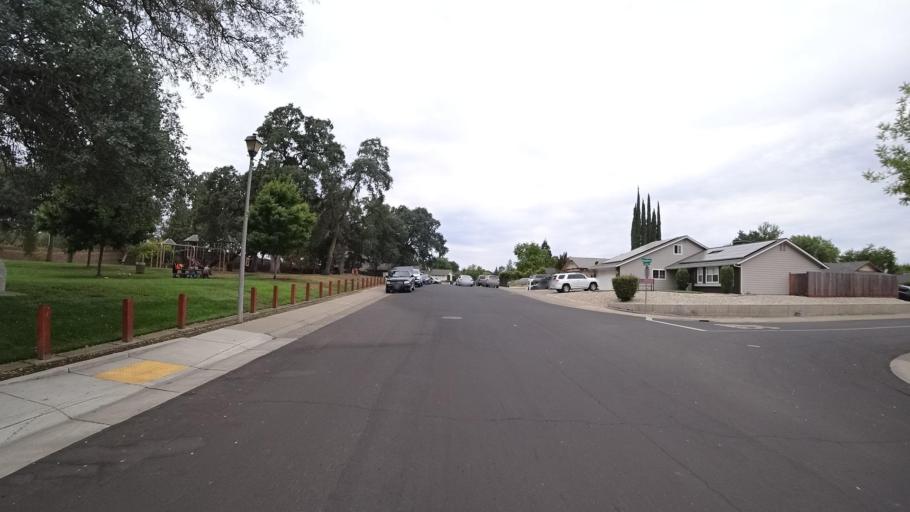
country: US
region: California
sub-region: Placer County
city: Rocklin
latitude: 38.7753
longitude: -121.2424
